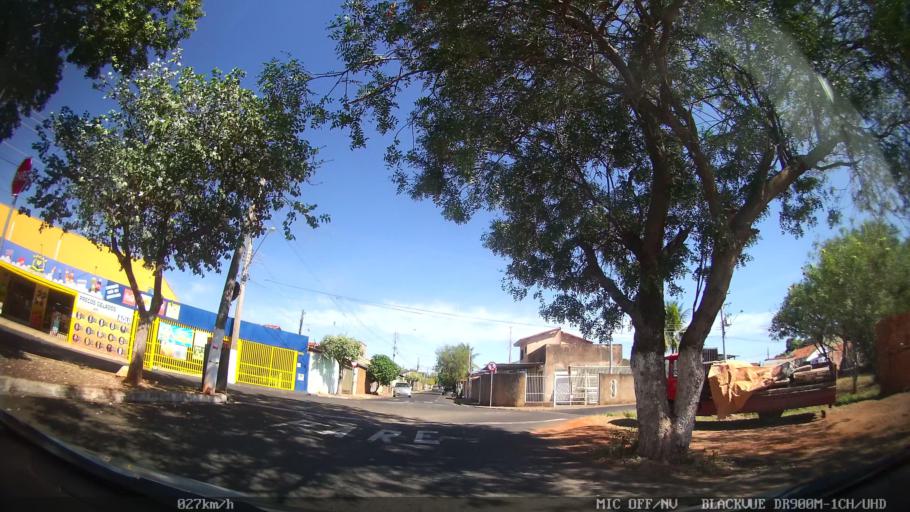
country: BR
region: Sao Paulo
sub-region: Sao Jose Do Rio Preto
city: Sao Jose do Rio Preto
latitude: -20.7670
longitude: -49.4081
